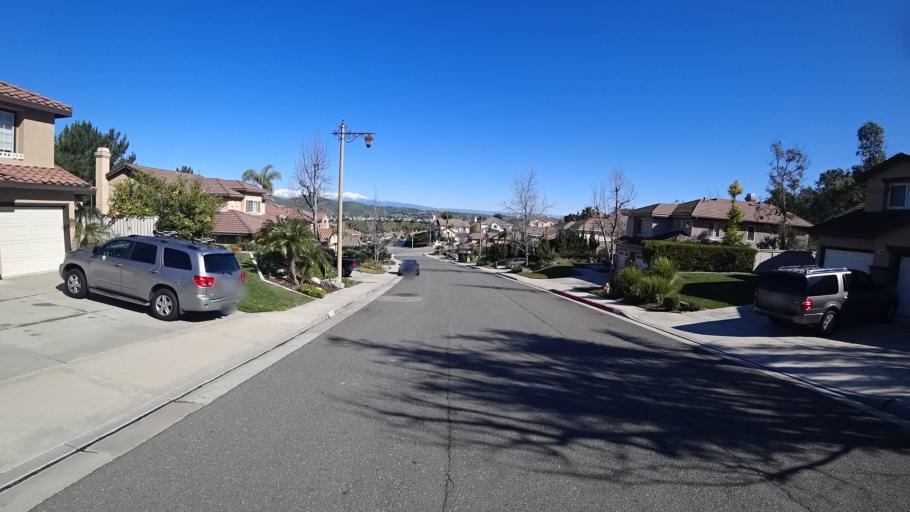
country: US
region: California
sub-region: Orange County
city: Yorba Linda
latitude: 33.8521
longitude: -117.7350
